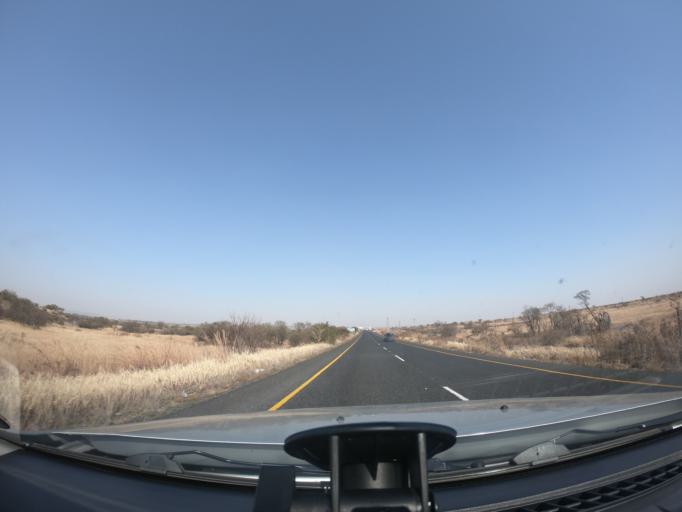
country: ZA
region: KwaZulu-Natal
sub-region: uThukela District Municipality
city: Ladysmith
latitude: -28.7239
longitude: 29.8116
